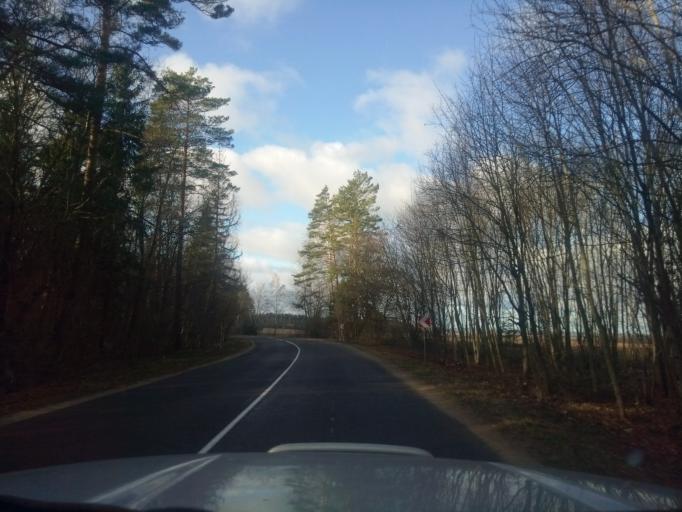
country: BY
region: Minsk
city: Kapyl'
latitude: 53.1760
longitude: 27.0087
